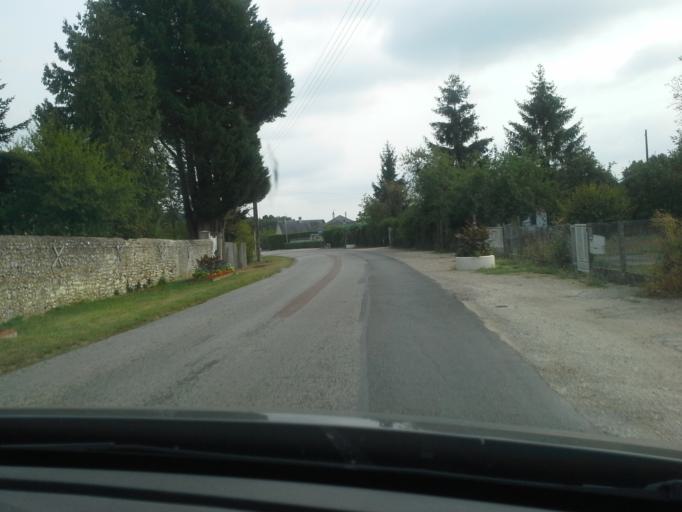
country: FR
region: Centre
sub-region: Departement du Loir-et-Cher
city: Herbault
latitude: 47.5882
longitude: 1.1999
